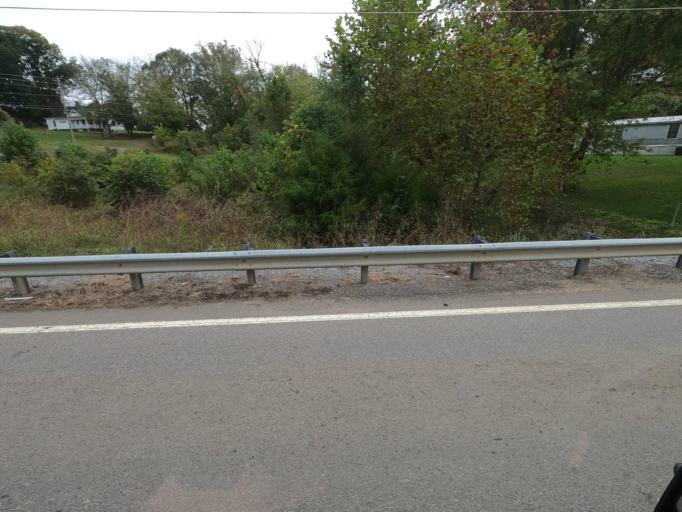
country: US
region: Tennessee
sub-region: Washington County
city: Jonesborough
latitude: 36.2493
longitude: -82.5439
